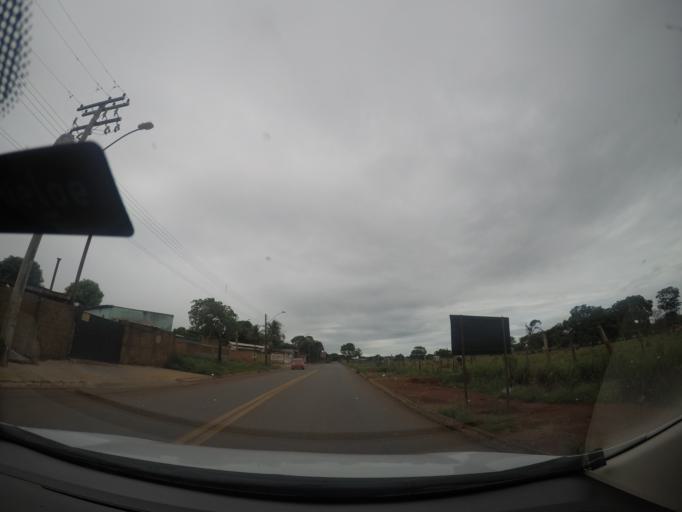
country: BR
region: Goias
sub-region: Goiania
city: Goiania
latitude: -16.6123
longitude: -49.3494
